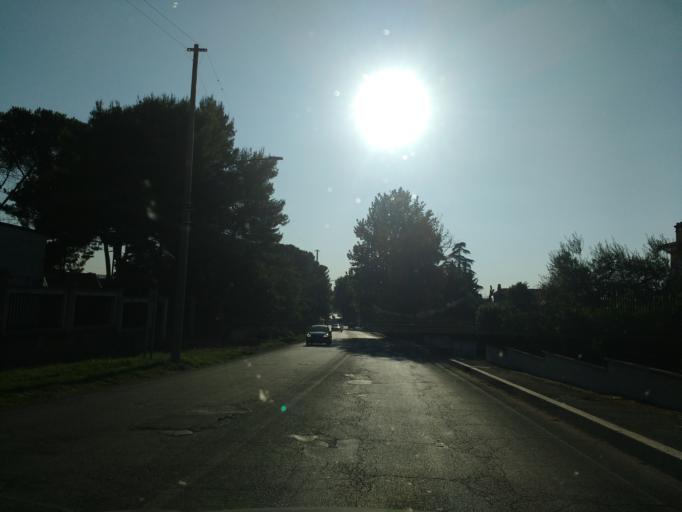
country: IT
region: Latium
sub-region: Citta metropolitana di Roma Capitale
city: Villa Adriana
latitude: 41.9565
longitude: 12.7823
